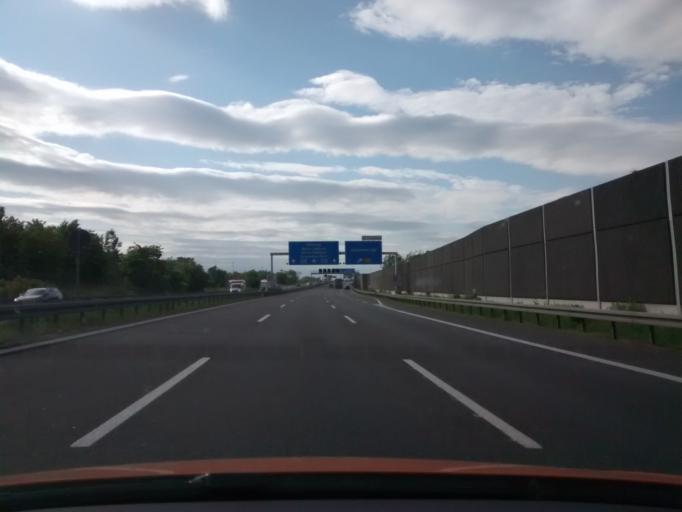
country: DE
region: Brandenburg
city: Schonefeld
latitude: 52.3888
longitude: 13.5280
